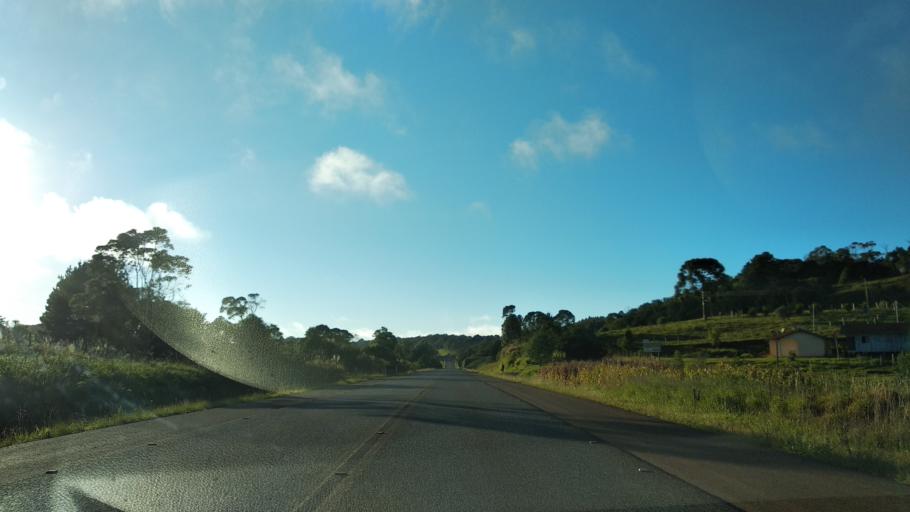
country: BR
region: Santa Catarina
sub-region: Correia Pinto
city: Correia Pinto
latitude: -27.6140
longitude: -50.6927
